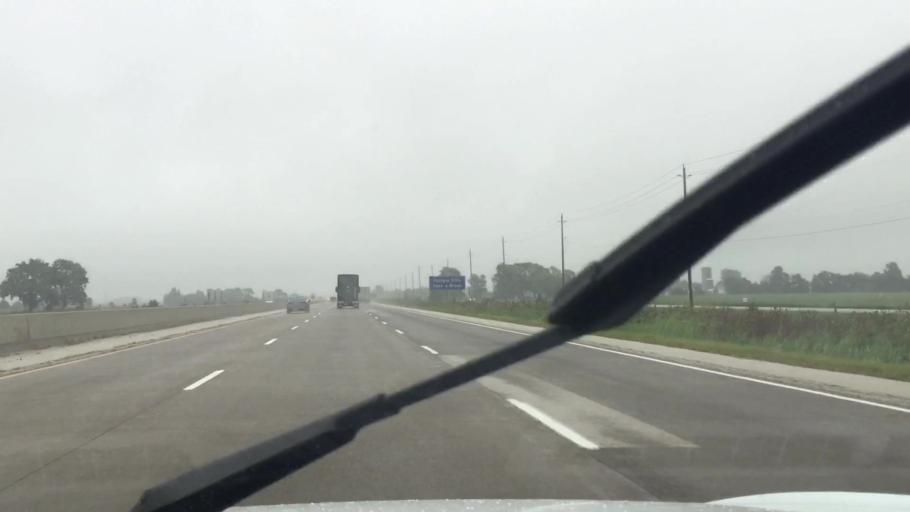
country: CA
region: Ontario
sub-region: Lambton County
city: Walpole Island
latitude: 42.2499
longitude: -82.5280
